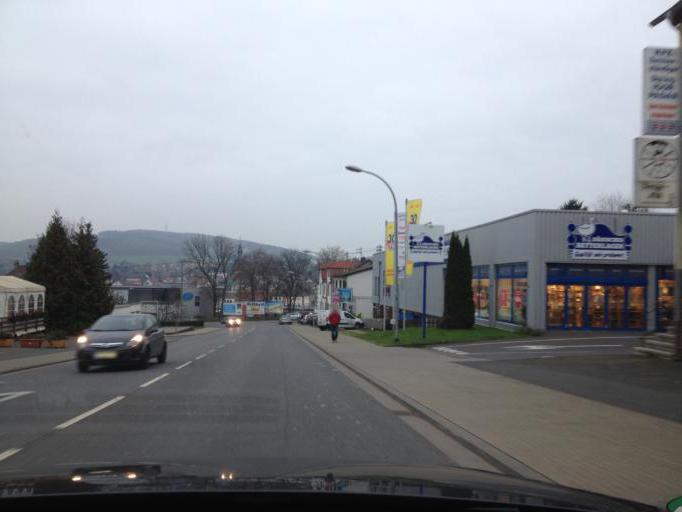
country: DE
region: Saarland
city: Sankt Wendel
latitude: 49.4667
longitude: 7.1618
